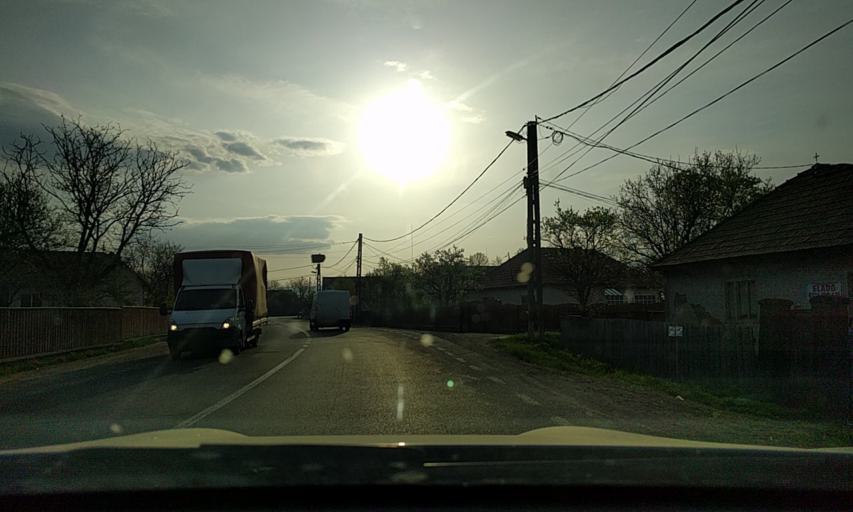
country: RO
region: Covasna
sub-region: Comuna Lemnia
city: Lemnia
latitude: 46.0448
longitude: 26.2580
